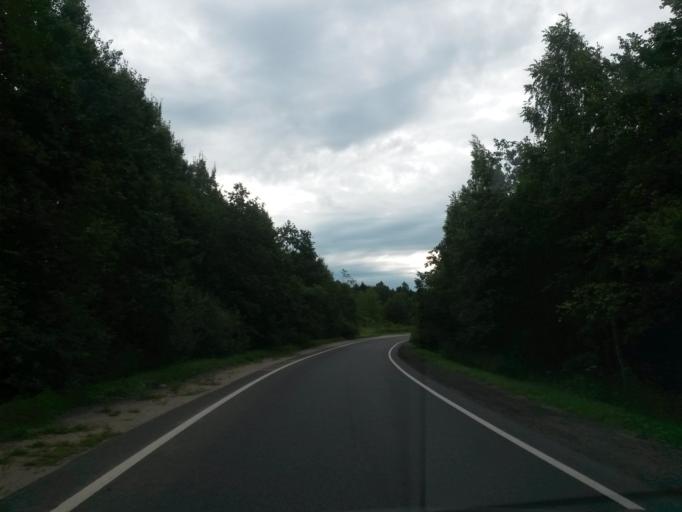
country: RU
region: Jaroslavl
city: Krasnyye Tkachi
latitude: 57.4037
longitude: 39.6577
